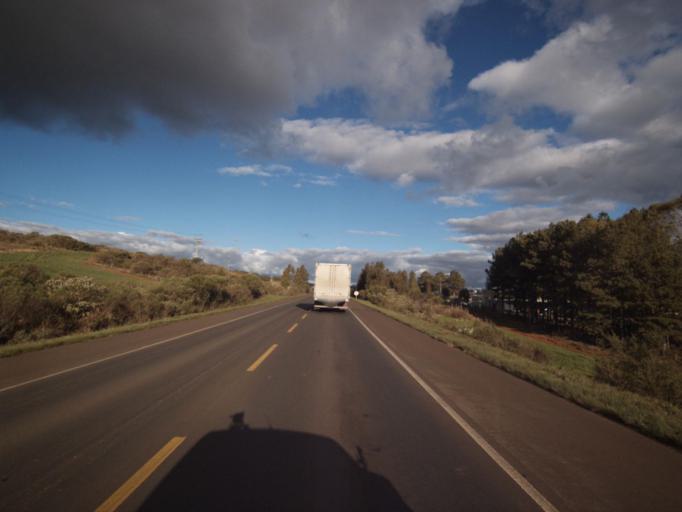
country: BR
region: Santa Catarina
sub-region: Campos Novos
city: Campos Novos
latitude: -27.3784
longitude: -51.2432
